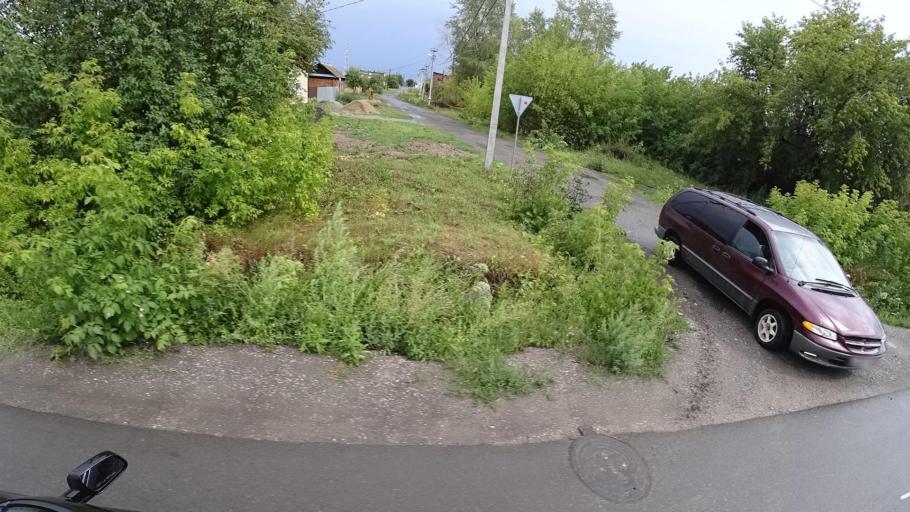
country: RU
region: Sverdlovsk
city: Kamyshlov
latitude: 56.8506
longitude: 62.7359
